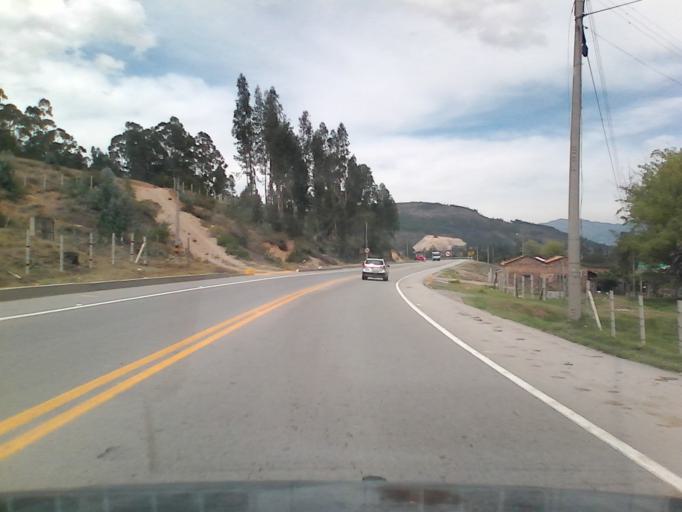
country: CO
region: Boyaca
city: Tibasosa
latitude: 5.7420
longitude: -72.9772
